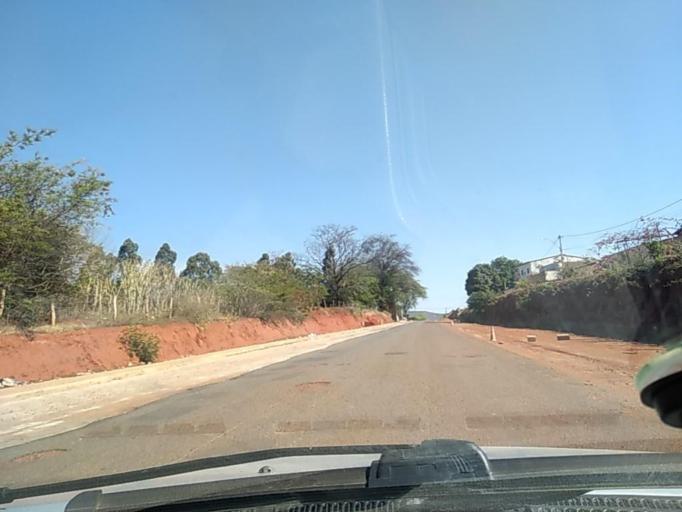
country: BR
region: Bahia
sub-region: Caetite
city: Caetite
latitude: -14.0514
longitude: -42.4848
